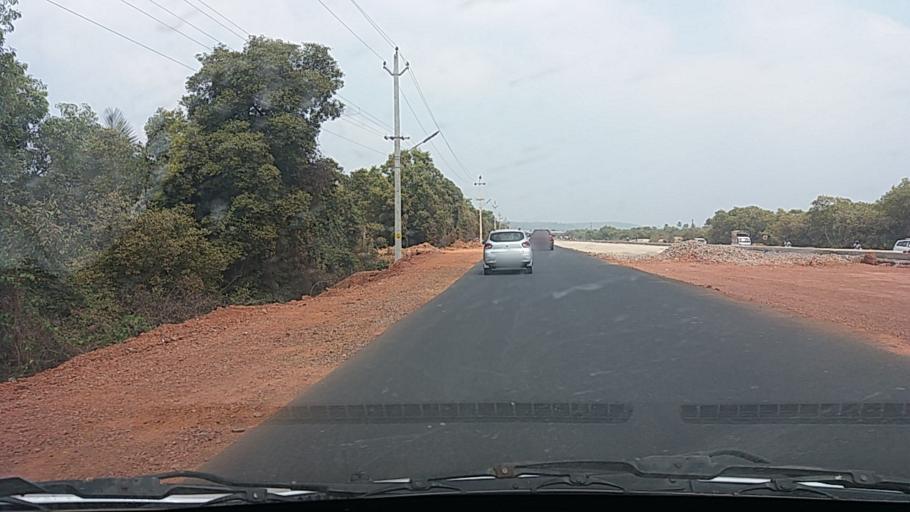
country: IN
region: Goa
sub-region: North Goa
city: Bambolim
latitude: 15.4820
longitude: 73.8474
